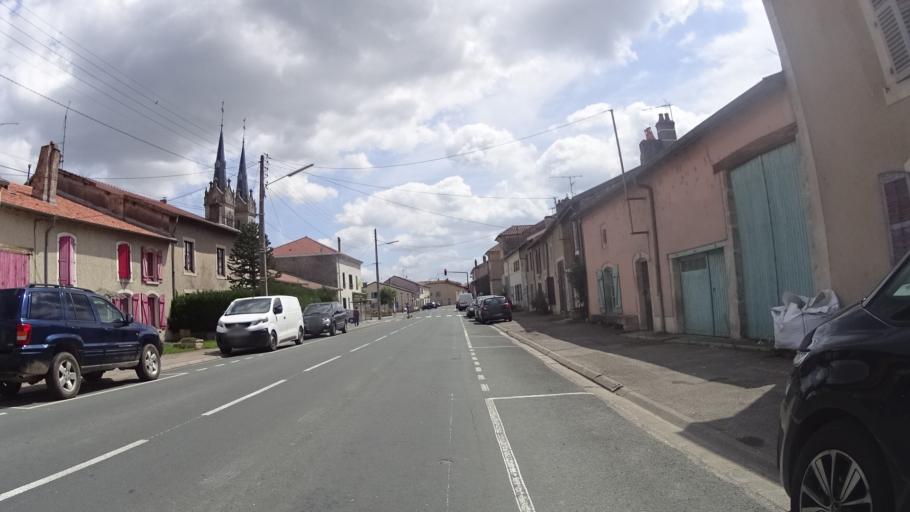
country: FR
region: Lorraine
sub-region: Departement de la Meuse
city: Euville
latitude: 48.7506
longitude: 5.6236
